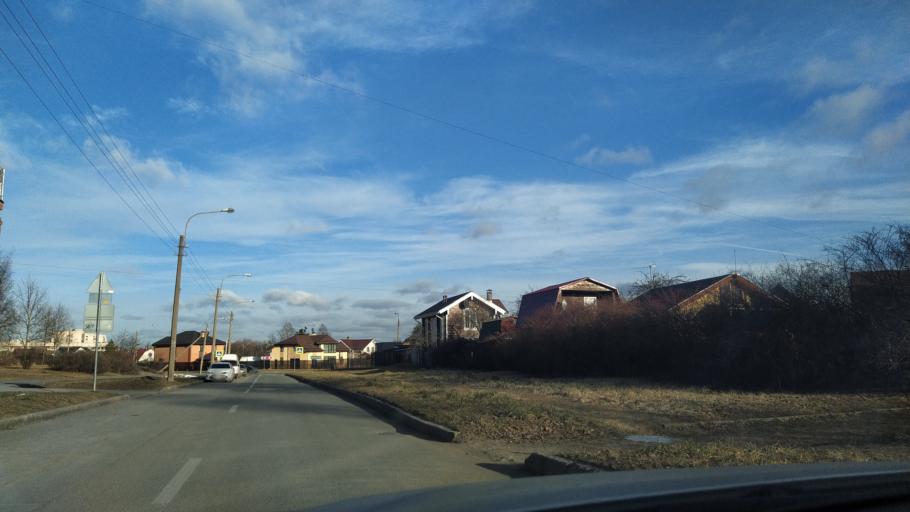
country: RU
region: St.-Petersburg
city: Pushkin
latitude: 59.7339
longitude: 30.4053
